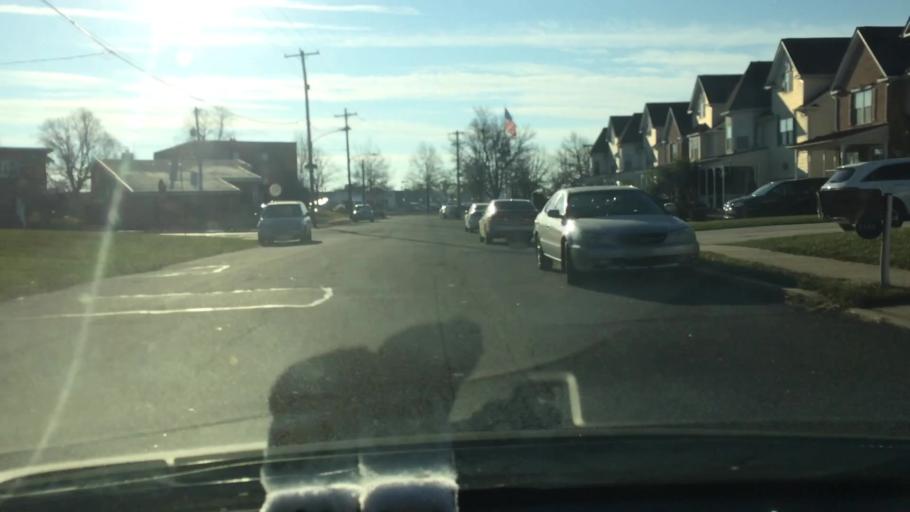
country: US
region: Pennsylvania
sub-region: Montgomery County
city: Rockledge
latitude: 40.0801
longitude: -75.0318
